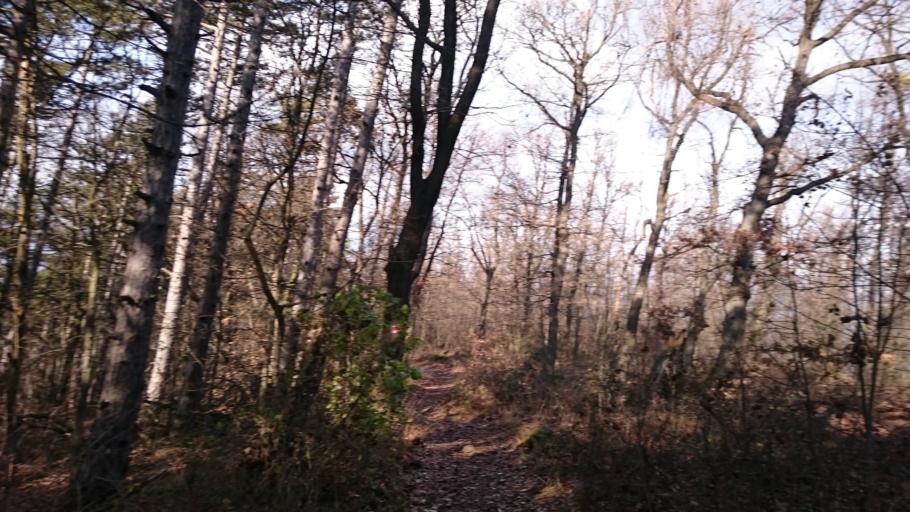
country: HU
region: Pest
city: Pilisborosjeno
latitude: 47.6155
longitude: 18.9972
